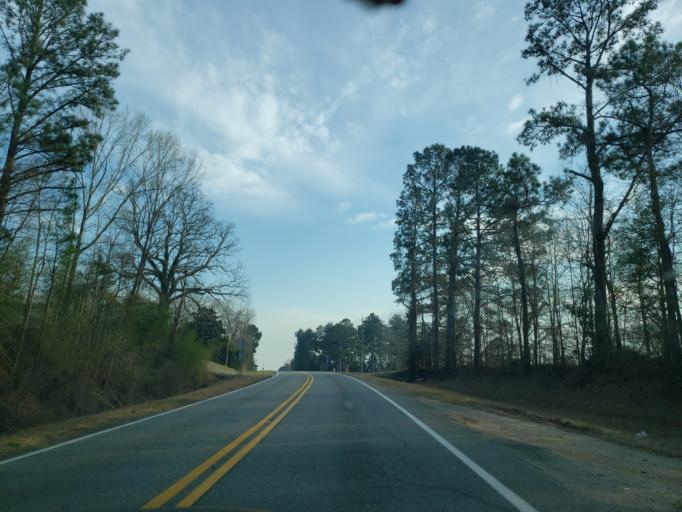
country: US
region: Alabama
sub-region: Hale County
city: Moundville
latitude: 32.9670
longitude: -87.6253
